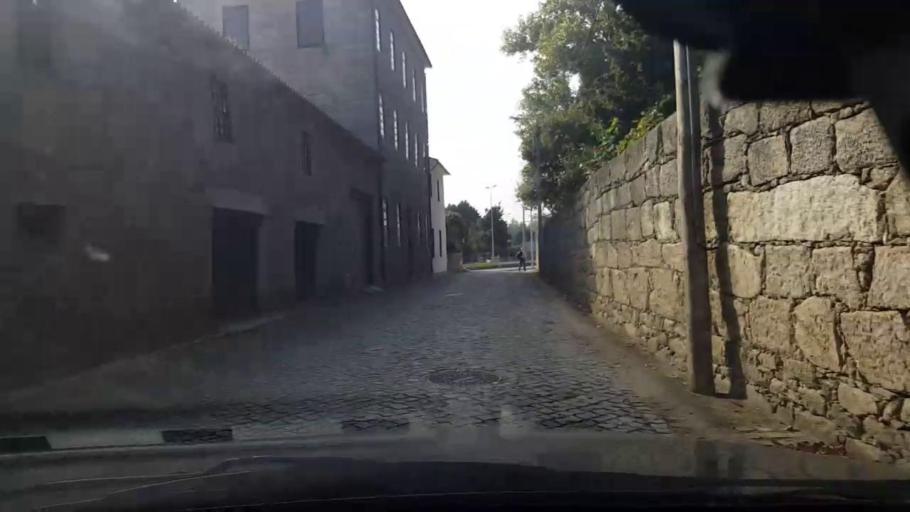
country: PT
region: Porto
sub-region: Maia
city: Gemunde
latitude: 41.2694
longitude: -8.6781
